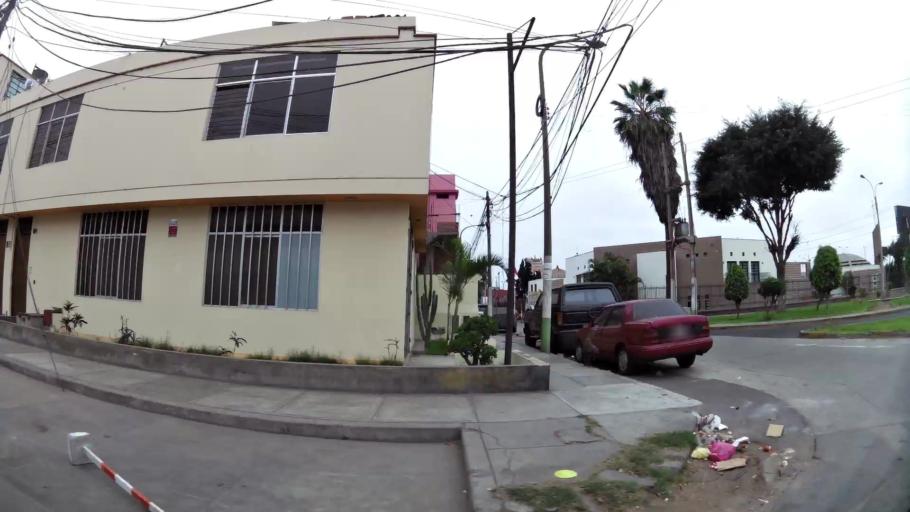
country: PE
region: Callao
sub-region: Callao
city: Callao
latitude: -12.0523
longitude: -77.0973
